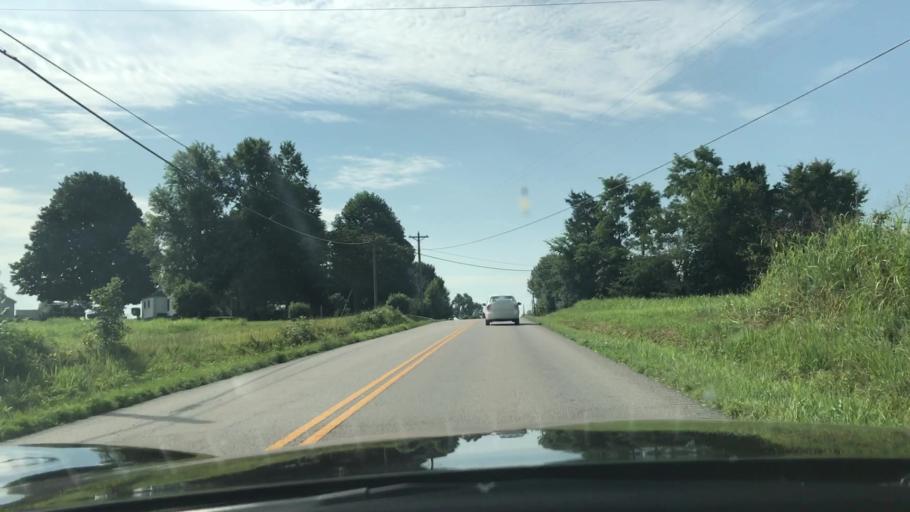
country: US
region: Kentucky
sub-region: Green County
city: Greensburg
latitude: 37.2655
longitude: -85.5619
